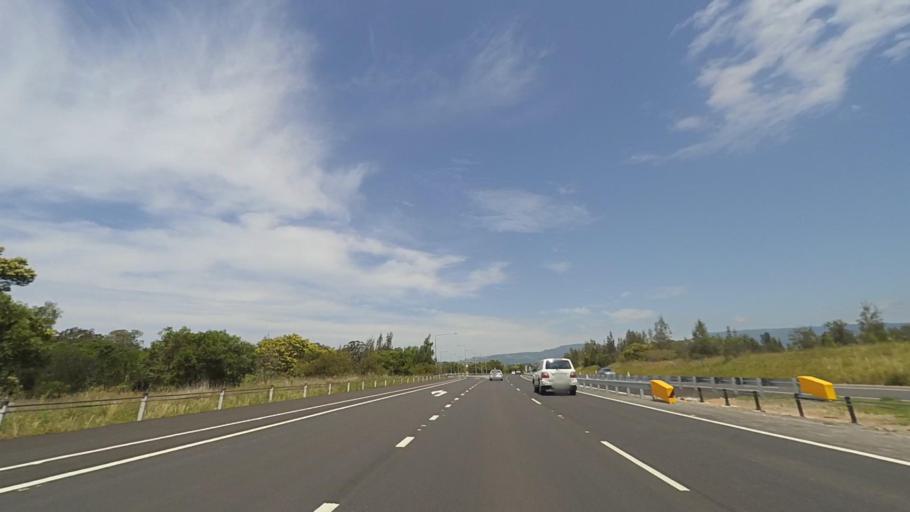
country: AU
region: New South Wales
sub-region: Shellharbour
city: Croom
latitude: -34.6290
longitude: 150.8359
